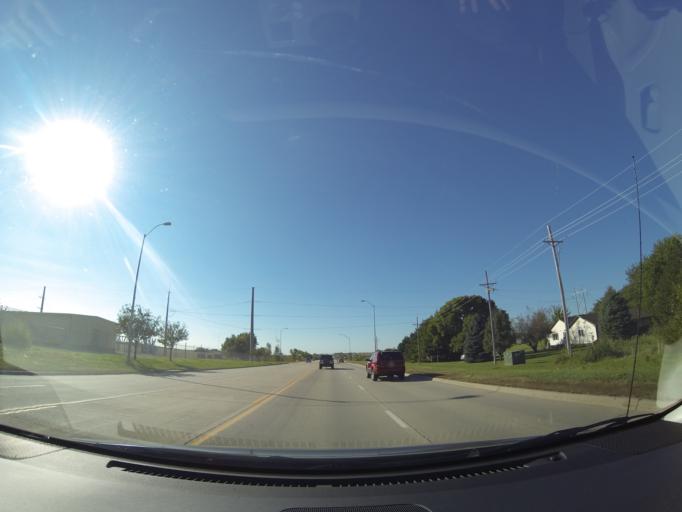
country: US
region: Nebraska
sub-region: Sarpy County
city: Gretna
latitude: 41.1261
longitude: -96.2534
